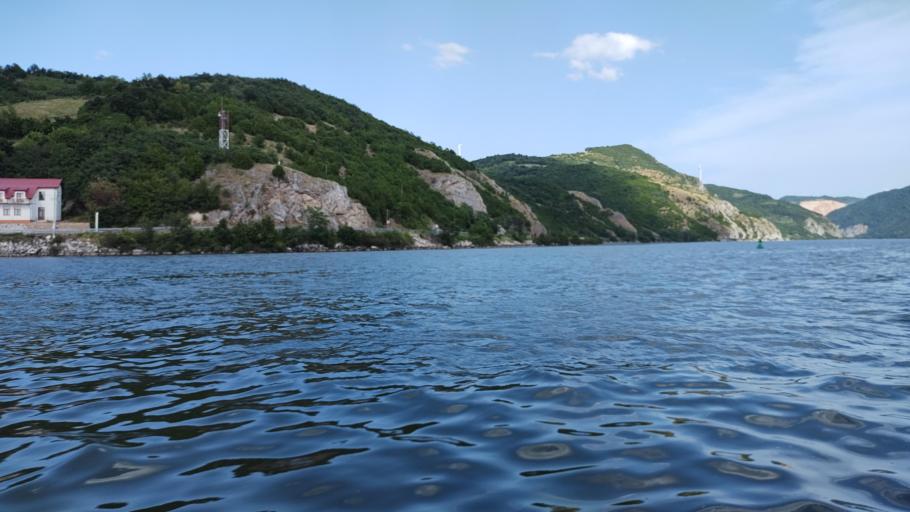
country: RO
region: Caras-Severin
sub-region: Comuna Pescari
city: Coronini
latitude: 44.6705
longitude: 21.6797
